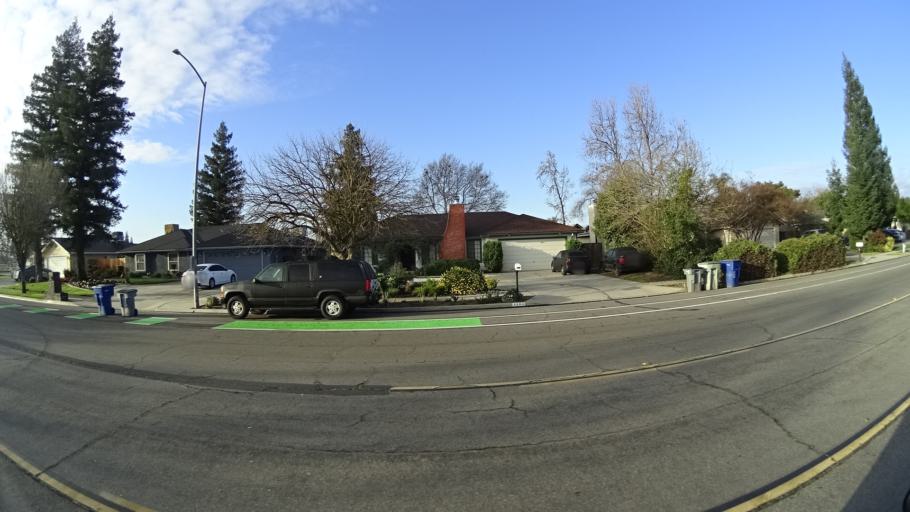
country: US
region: California
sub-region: Fresno County
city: West Park
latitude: 36.8136
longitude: -119.8728
